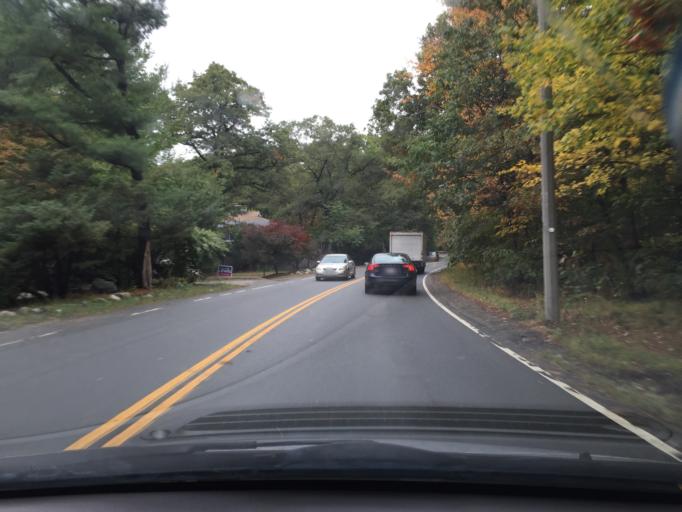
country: US
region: Massachusetts
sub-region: Middlesex County
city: Winchester
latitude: 42.4424
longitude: -71.1240
